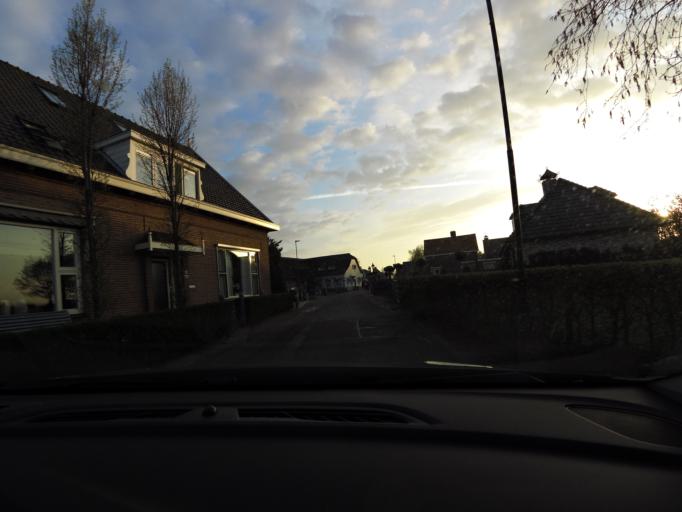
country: NL
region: South Holland
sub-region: Gemeente Giessenlanden
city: Giessenburg
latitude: 51.8543
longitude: 4.8947
